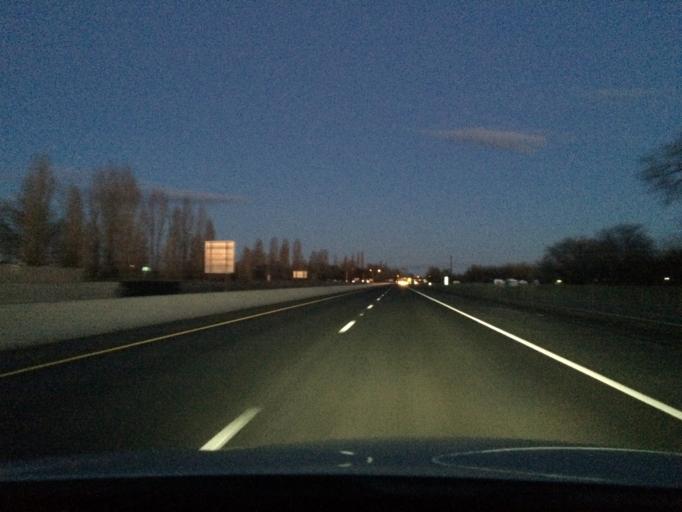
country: US
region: Washington
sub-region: Grant County
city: Cascade Valley
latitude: 47.1039
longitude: -119.3382
